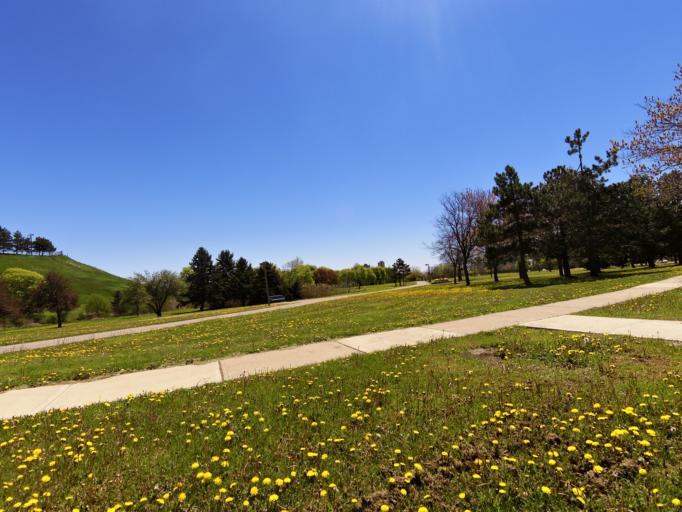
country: CA
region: Ontario
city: Brampton
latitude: 43.7264
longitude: -79.7278
